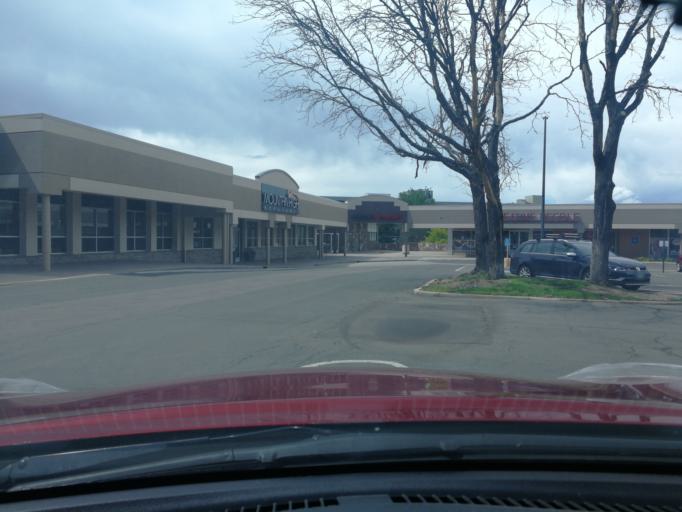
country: US
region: Colorado
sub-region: Arapahoe County
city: Littleton
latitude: 39.5908
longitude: -104.9908
